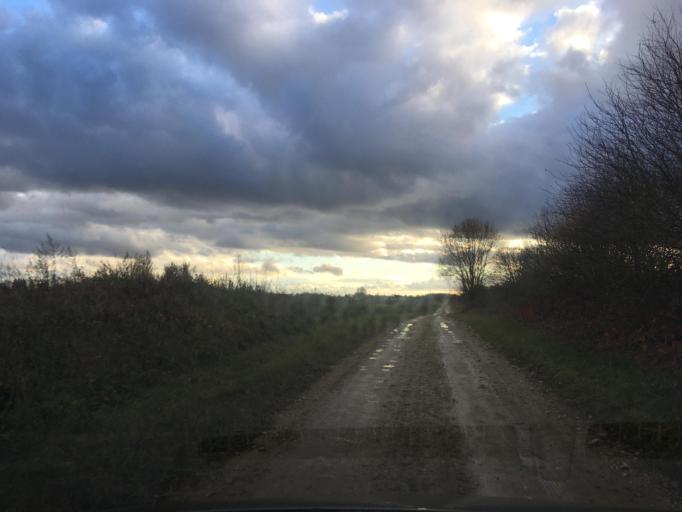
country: EE
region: Harju
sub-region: Raasiku vald
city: Arukula
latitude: 59.3523
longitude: 25.1077
